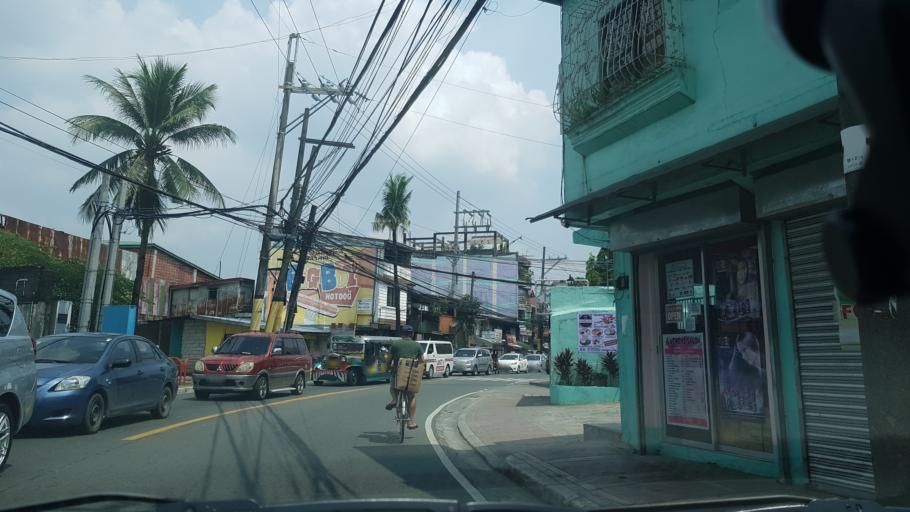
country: PH
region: Metro Manila
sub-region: Marikina
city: Calumpang
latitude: 14.6417
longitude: 121.0942
